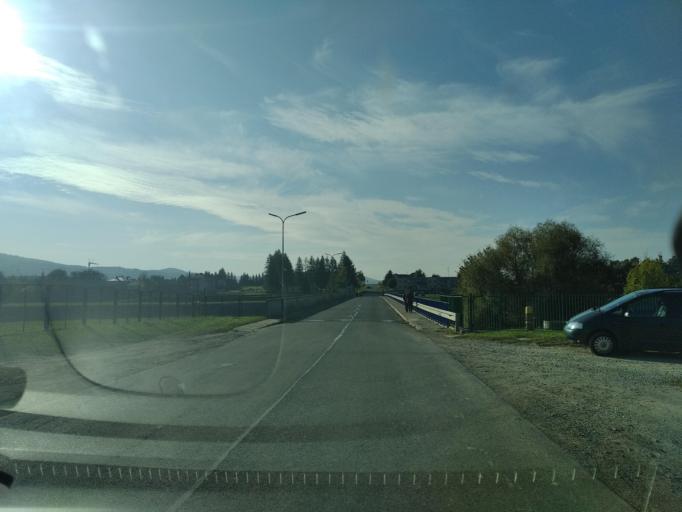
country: PL
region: Subcarpathian Voivodeship
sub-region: Powiat krosnienski
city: Sieniawa
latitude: 49.5652
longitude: 21.9329
